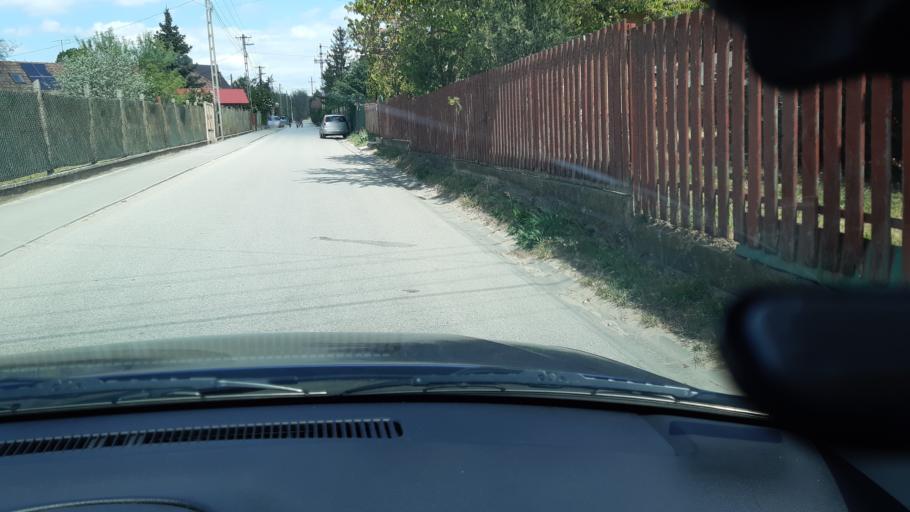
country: HU
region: Pest
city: Nagytarcsa
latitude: 47.5318
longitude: 19.2829
